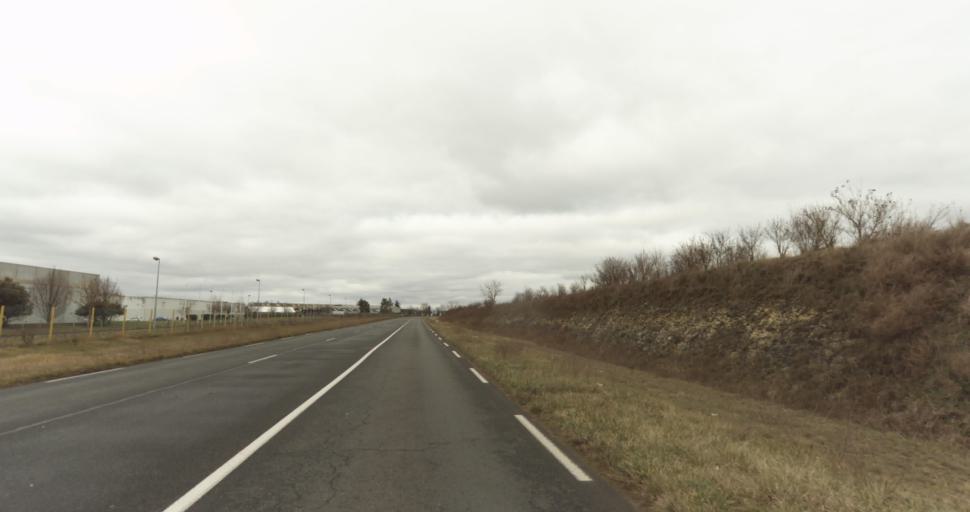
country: FR
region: Pays de la Loire
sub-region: Departement de Maine-et-Loire
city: Varrains
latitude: 47.2104
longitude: -0.0550
